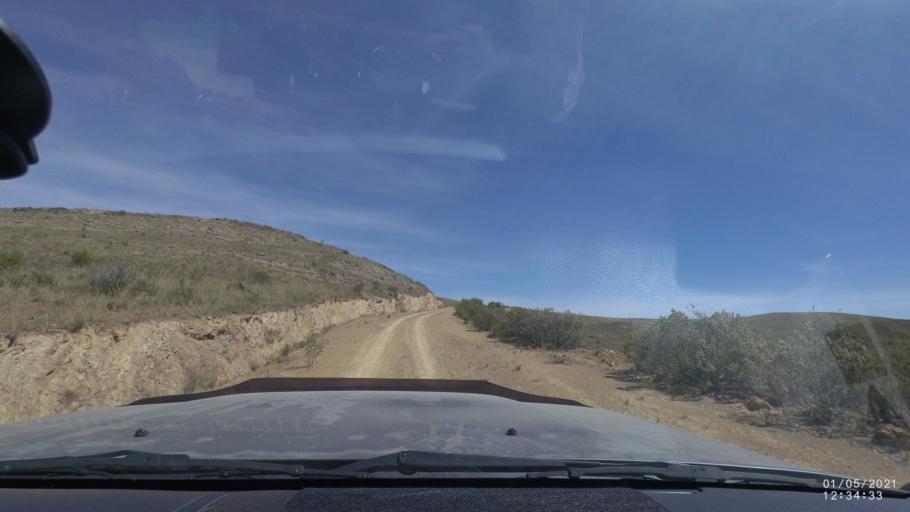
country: BO
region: Cochabamba
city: Capinota
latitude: -17.6770
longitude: -66.1516
